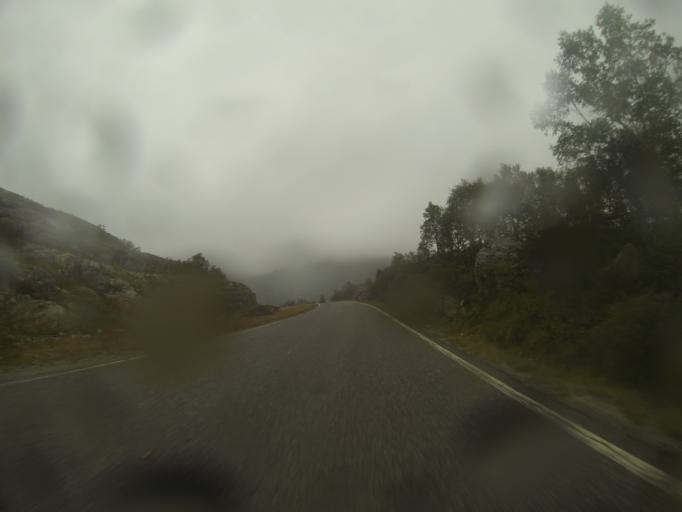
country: NO
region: Vest-Agder
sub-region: Sirdal
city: Tonstad
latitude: 58.9125
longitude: 6.7471
